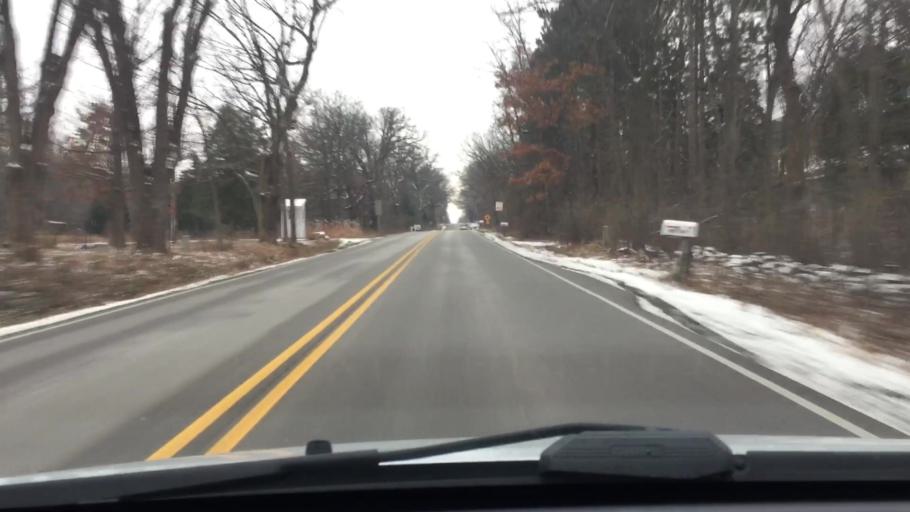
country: US
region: Wisconsin
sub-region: Waukesha County
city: Delafield
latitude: 43.0317
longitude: -88.4042
